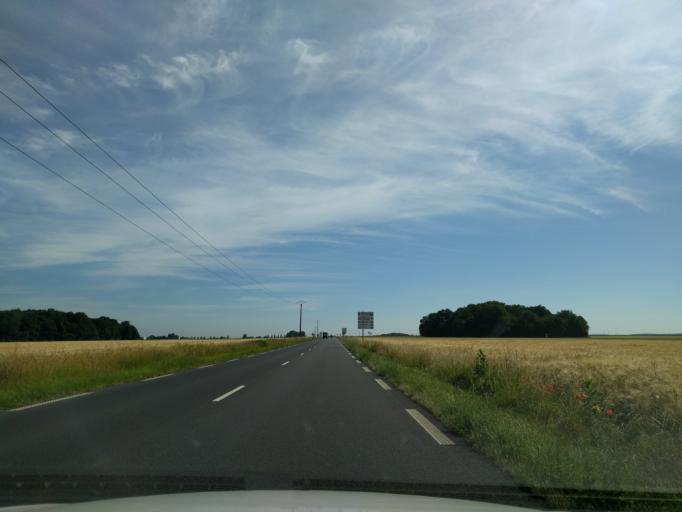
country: FR
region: Picardie
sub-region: Departement de l'Oise
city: Tille
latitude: 49.5059
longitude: 2.1694
